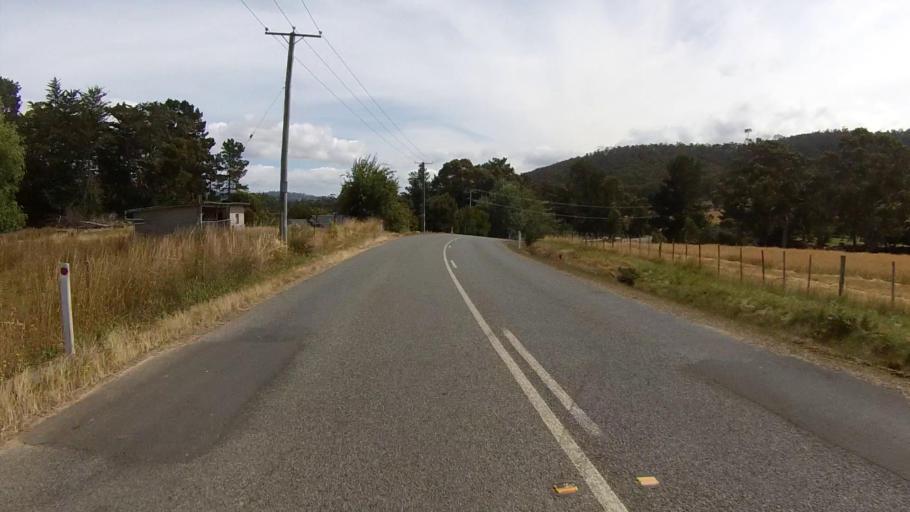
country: AU
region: Tasmania
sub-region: Huon Valley
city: Cygnet
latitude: -43.2119
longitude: 147.1163
